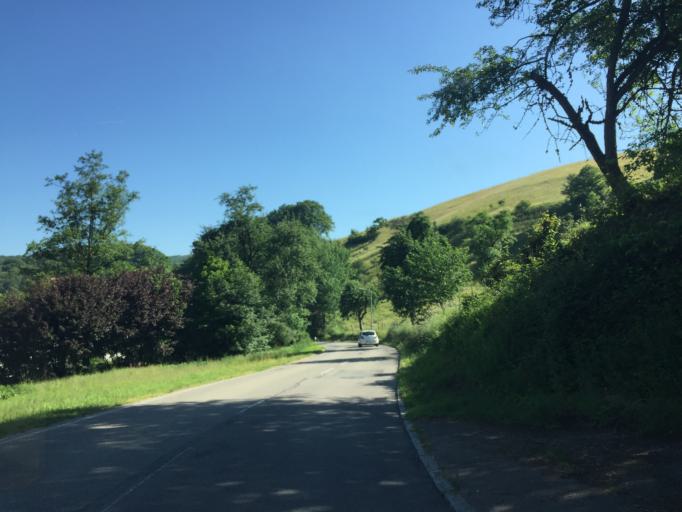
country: DE
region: Hesse
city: Unter-Abtsteinach
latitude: 49.5234
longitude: 8.7452
